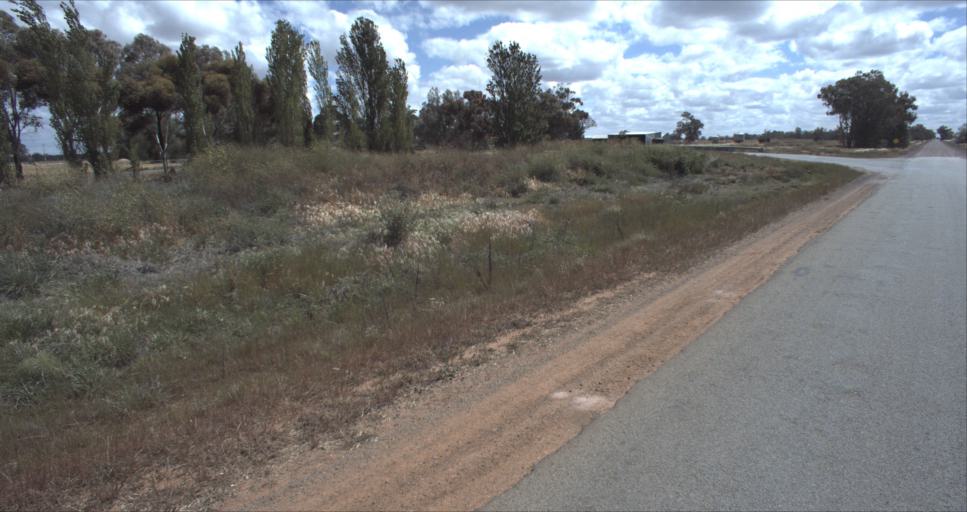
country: AU
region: New South Wales
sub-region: Leeton
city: Leeton
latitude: -34.5878
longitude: 146.3624
